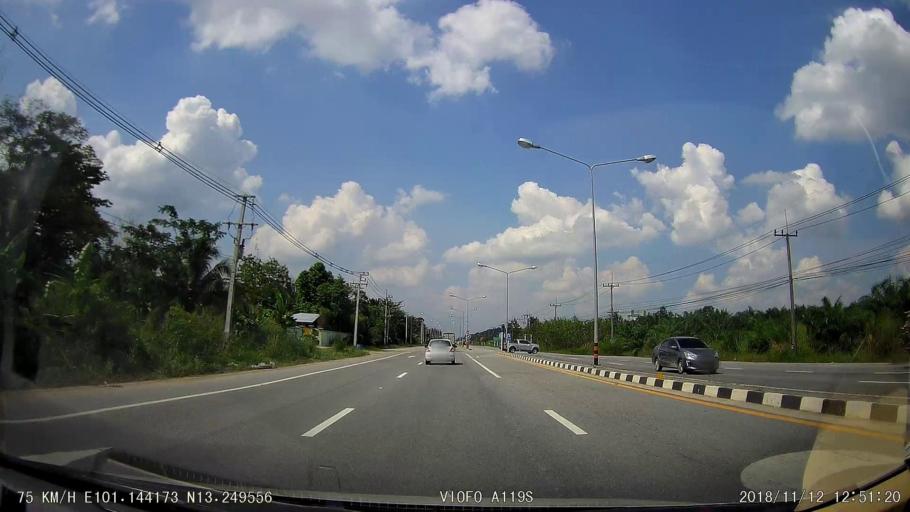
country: TH
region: Chon Buri
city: Ban Bueng
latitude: 13.2497
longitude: 101.1441
